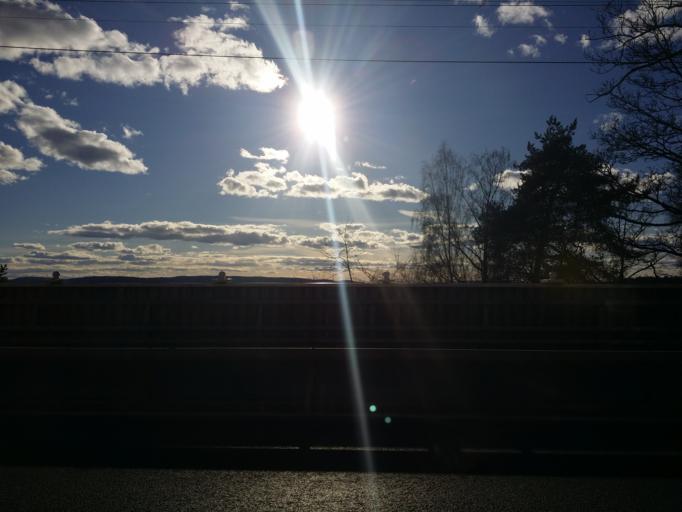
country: NO
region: Akershus
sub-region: Oppegard
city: Kolbotn
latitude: 59.8604
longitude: 10.7856
